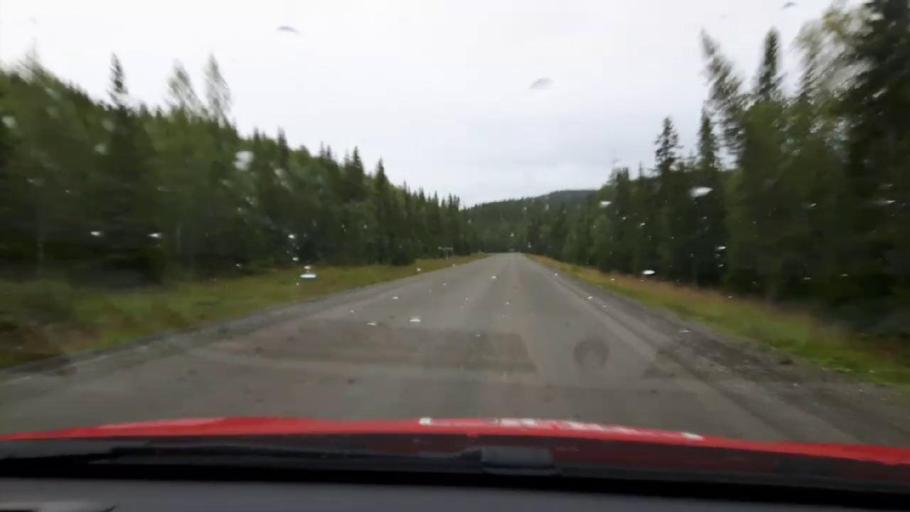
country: SE
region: Jaemtland
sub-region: Are Kommun
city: Are
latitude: 63.4261
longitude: 12.7398
